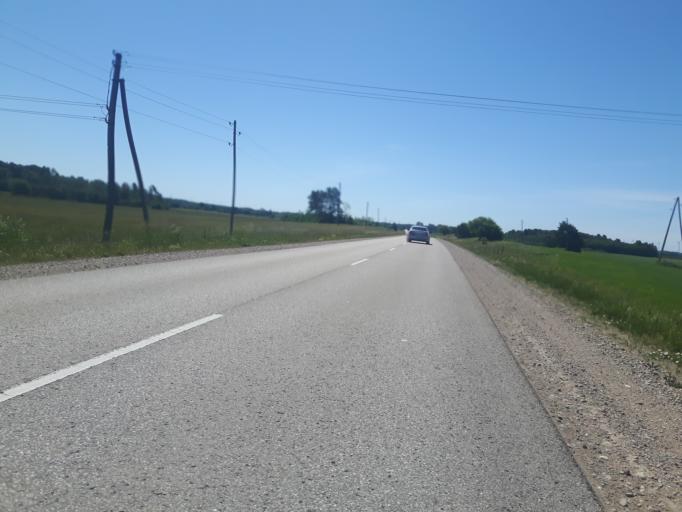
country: LV
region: Durbe
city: Liegi
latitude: 56.5803
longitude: 21.2701
